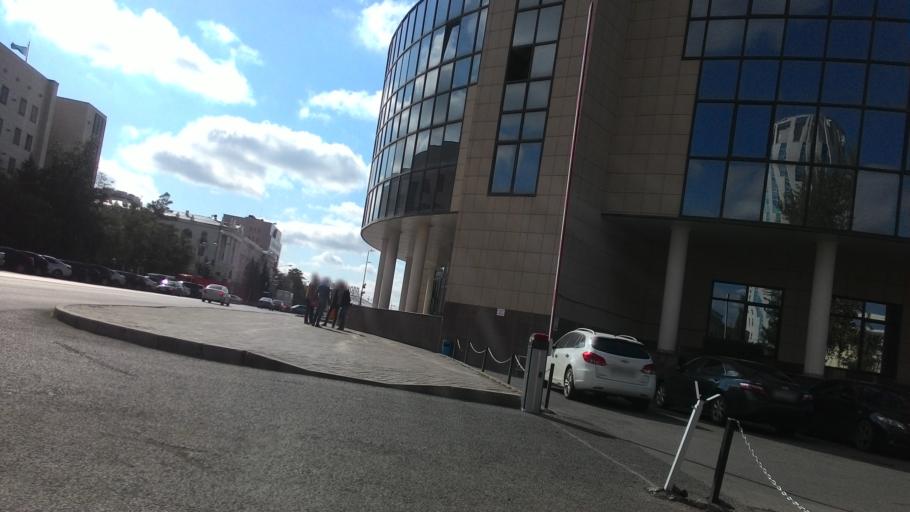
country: KZ
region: Astana Qalasy
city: Astana
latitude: 51.1690
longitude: 71.4204
